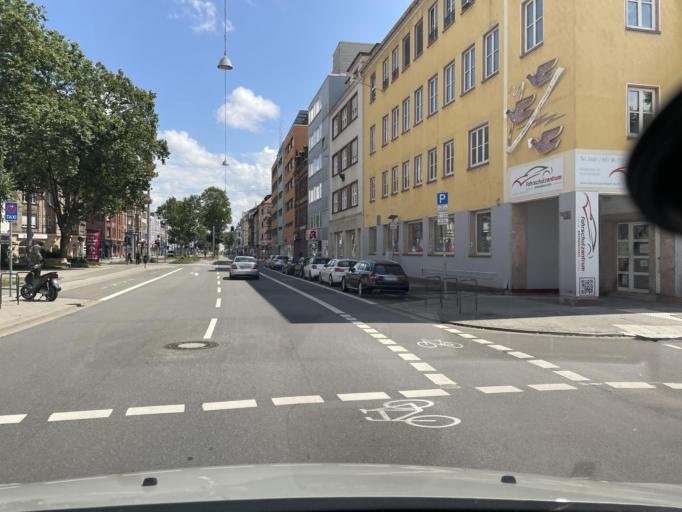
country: DE
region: Saarland
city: Saarbrucken
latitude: 49.2295
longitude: 7.0085
